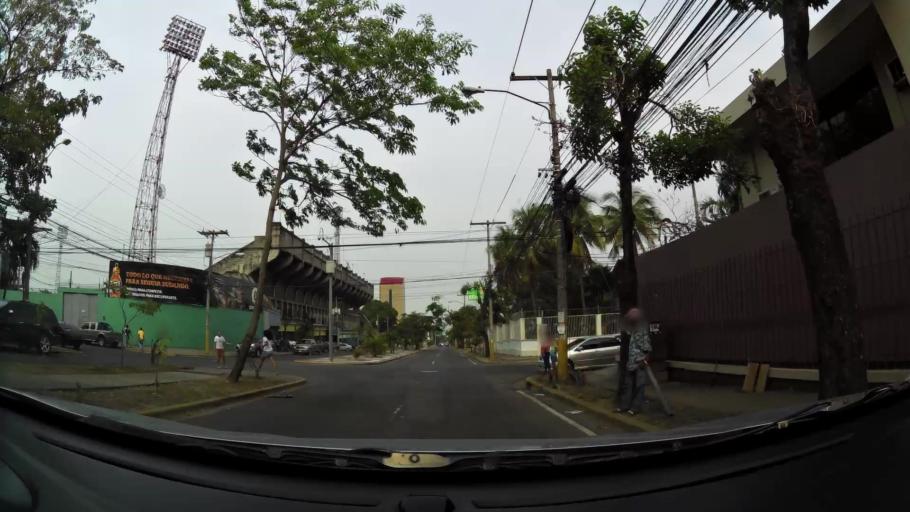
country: HN
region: Cortes
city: San Pedro Sula
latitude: 15.5066
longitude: -88.0343
